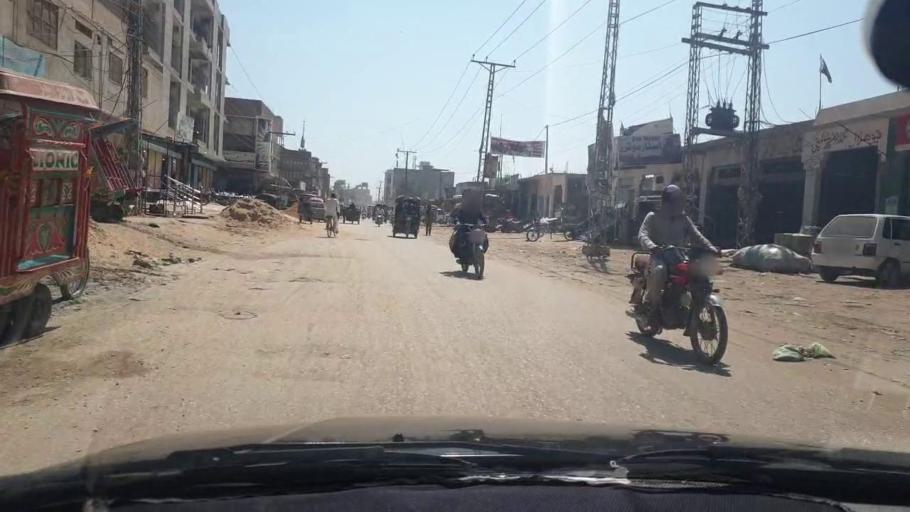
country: PK
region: Sindh
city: Tando Allahyar
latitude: 25.4611
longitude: 68.7156
